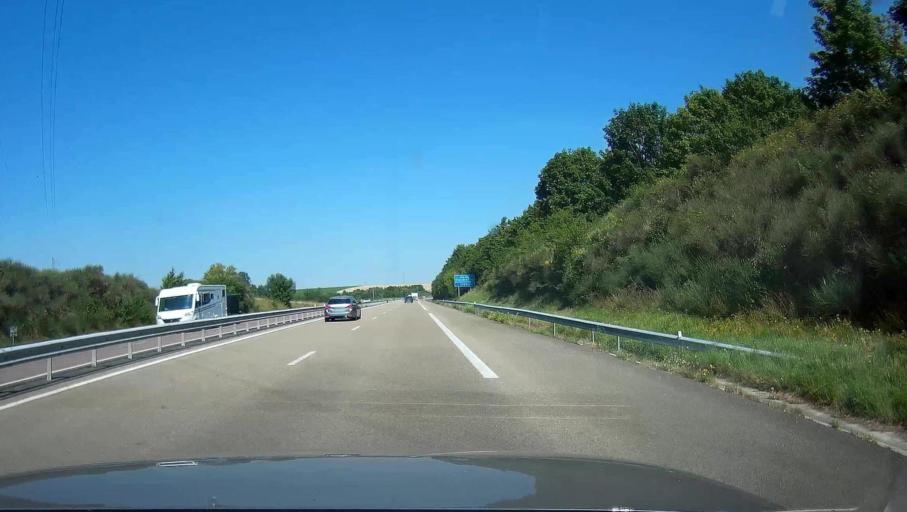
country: FR
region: Champagne-Ardenne
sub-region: Departement de l'Aube
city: Creney-pres-Troyes
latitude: 48.3072
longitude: 4.1653
